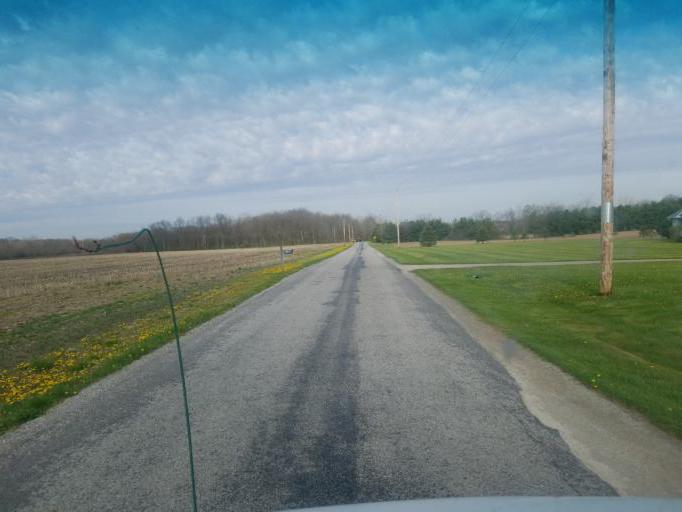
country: US
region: Ohio
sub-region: Delaware County
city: Ashley
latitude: 40.4343
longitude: -83.0356
